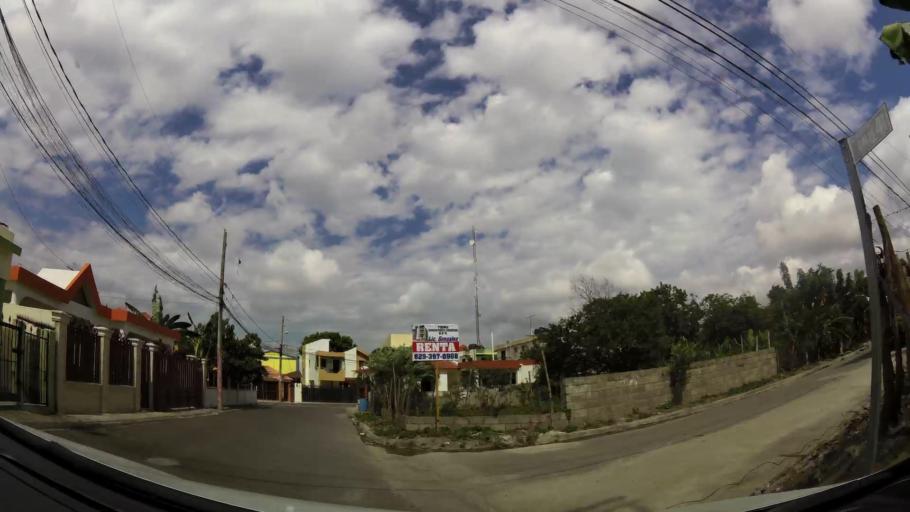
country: DO
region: Santiago
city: Santiago de los Caballeros
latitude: 19.4709
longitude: -70.6990
